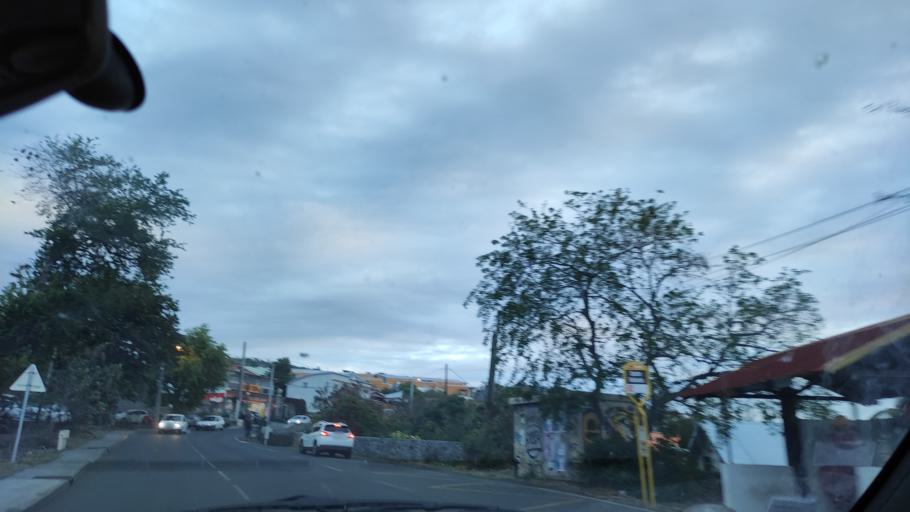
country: RE
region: Reunion
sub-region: Reunion
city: Saint-Leu
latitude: -21.1968
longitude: 55.2920
